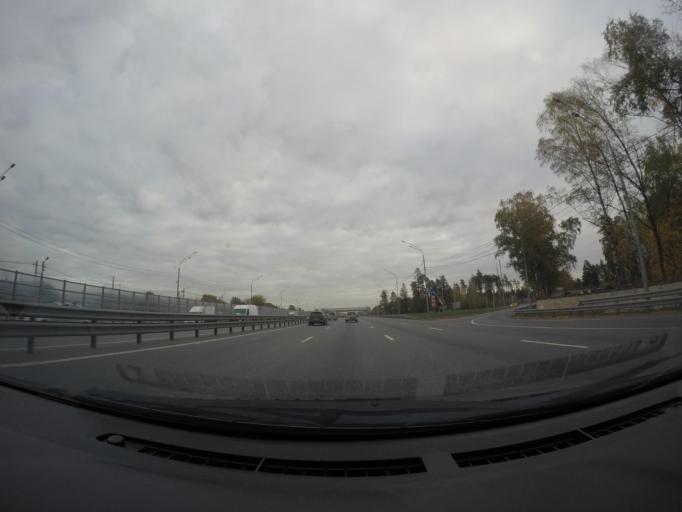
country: RU
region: Moskovskaya
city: Zheleznodorozhnyy
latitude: 55.8025
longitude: 38.0178
